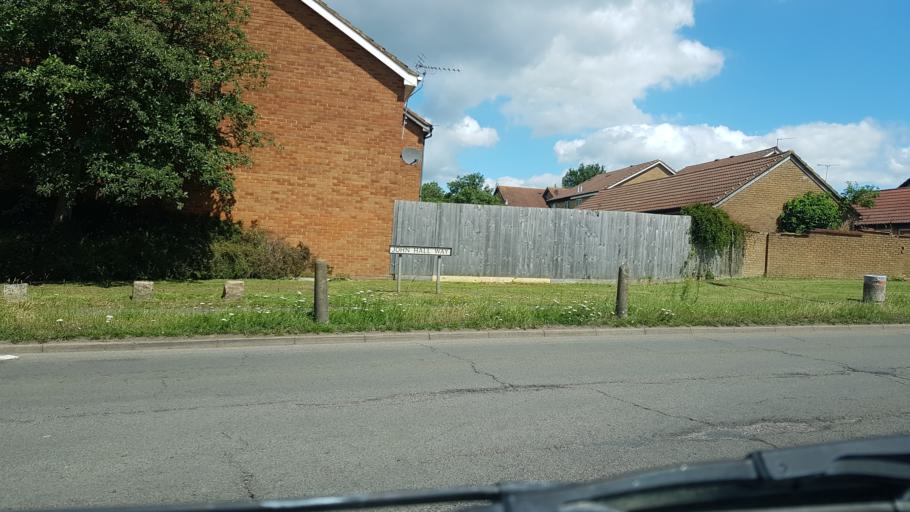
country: GB
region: England
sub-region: Buckinghamshire
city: High Wycombe
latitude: 51.6138
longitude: -0.7727
